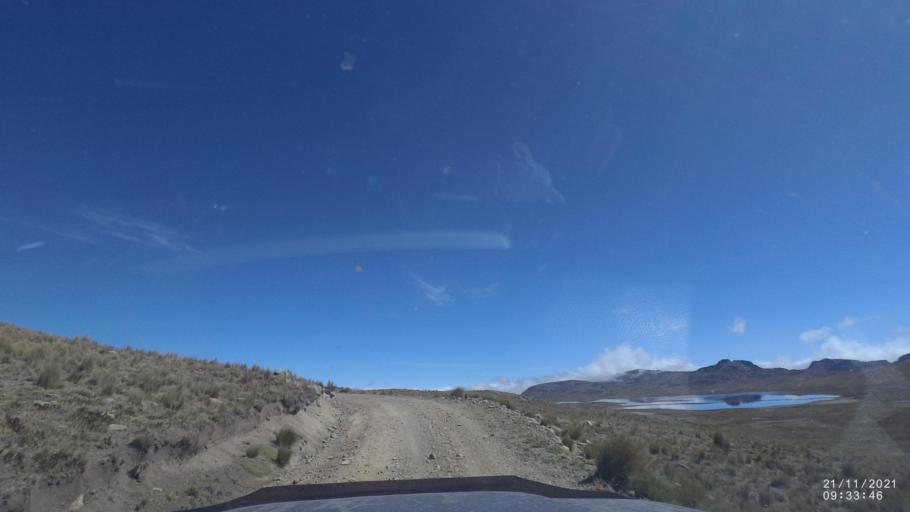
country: BO
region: Cochabamba
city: Cochabamba
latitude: -17.0591
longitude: -66.2579
